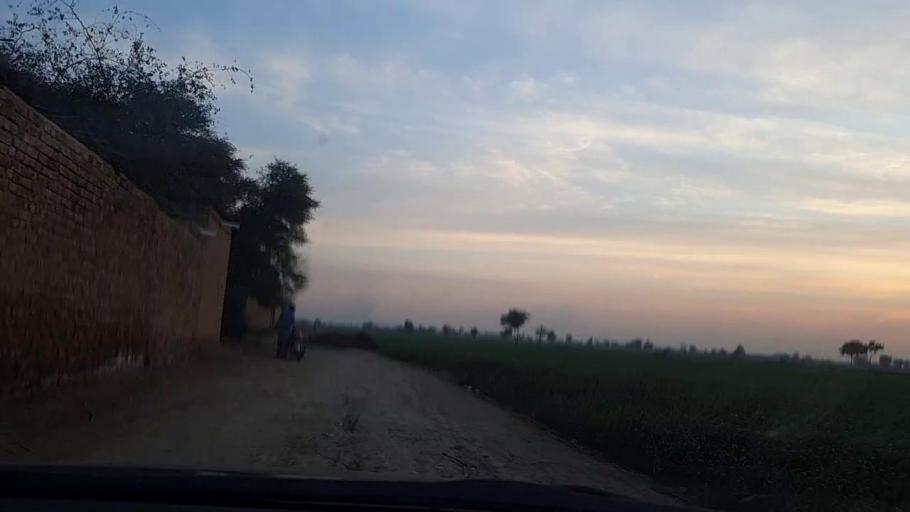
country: PK
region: Sindh
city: Sakrand
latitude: 26.2010
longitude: 68.3183
